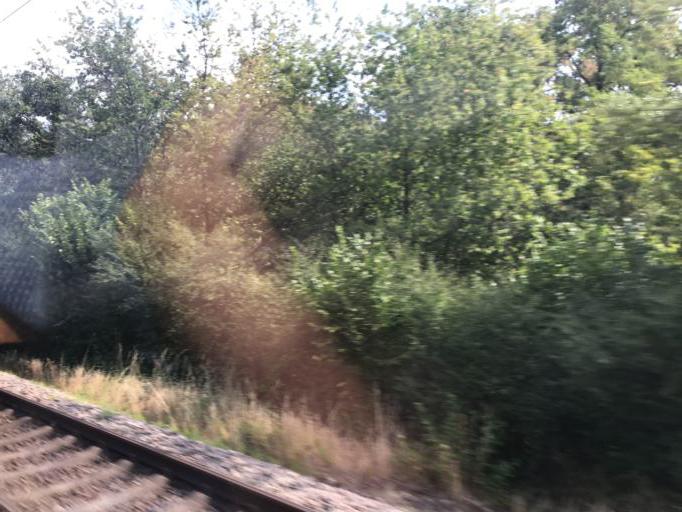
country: DE
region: Saarland
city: Ottweiler
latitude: 49.3791
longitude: 7.1737
